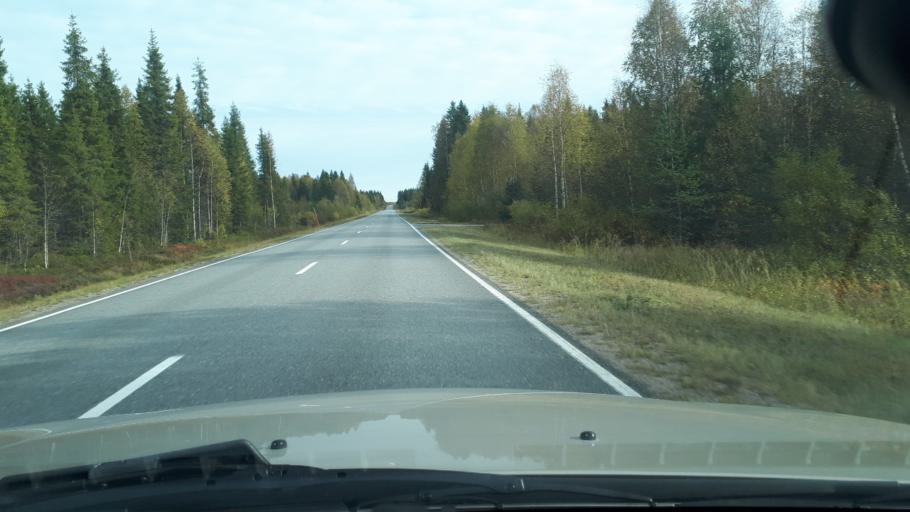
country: FI
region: Lapland
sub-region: Rovaniemi
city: Ranua
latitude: 65.9697
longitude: 26.0968
